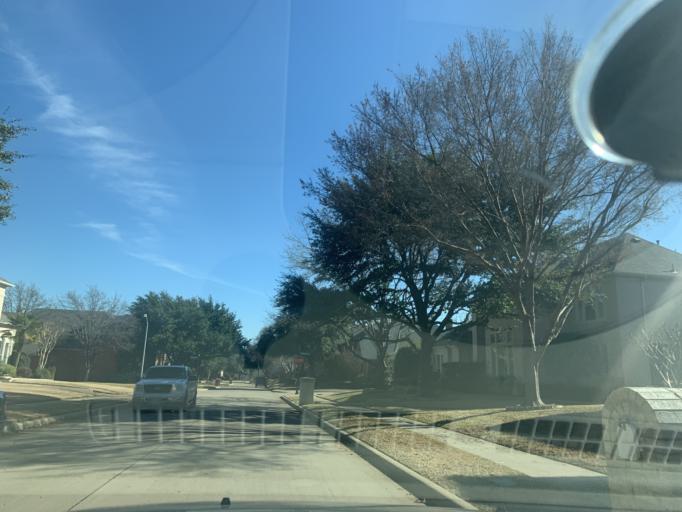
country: US
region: Texas
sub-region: Denton County
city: The Colony
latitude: 33.0520
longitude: -96.8150
